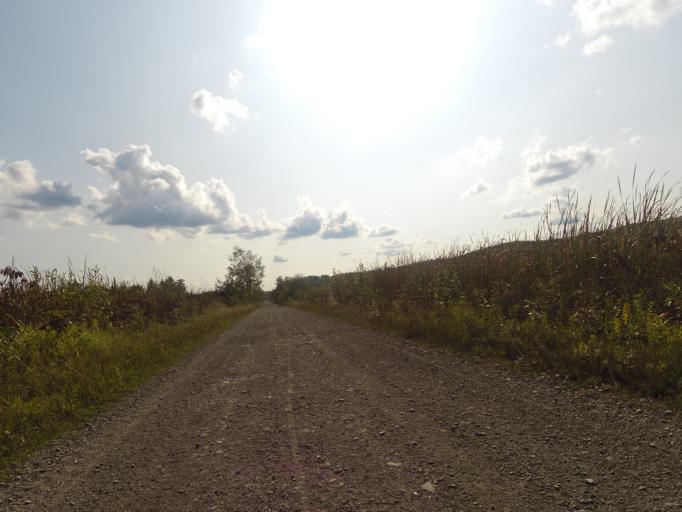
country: CA
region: Ontario
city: Renfrew
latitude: 45.1340
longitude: -76.6867
